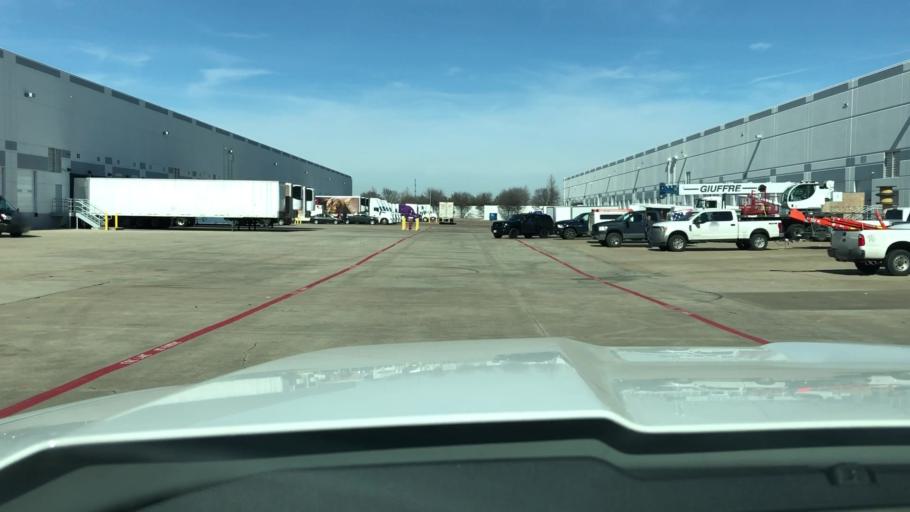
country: US
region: Texas
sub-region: Dallas County
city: Coppell
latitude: 32.9441
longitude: -96.9950
